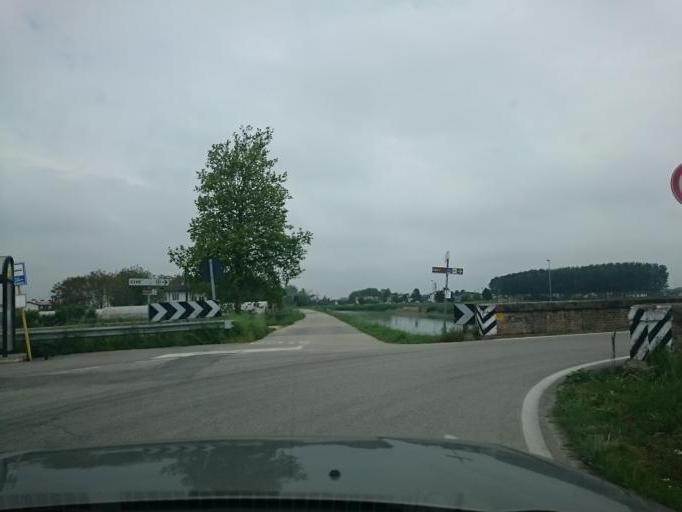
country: IT
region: Veneto
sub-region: Provincia di Venezia
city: Valli
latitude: 45.2113
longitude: 12.1426
